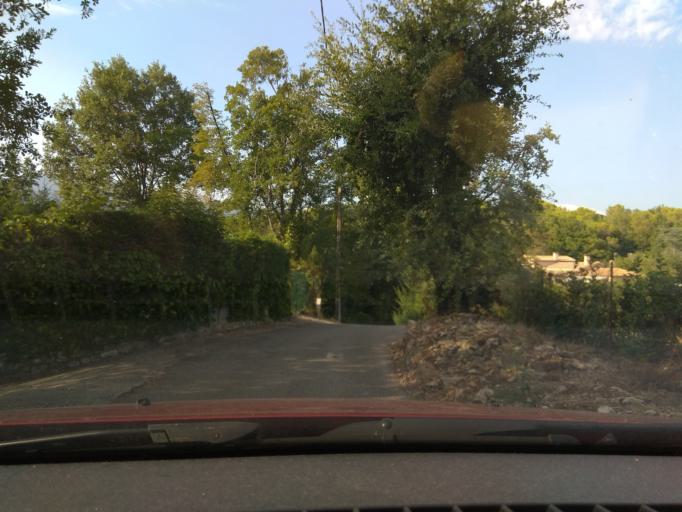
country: FR
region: Provence-Alpes-Cote d'Azur
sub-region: Departement des Alpes-Maritimes
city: Le Rouret
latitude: 43.6693
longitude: 7.0474
